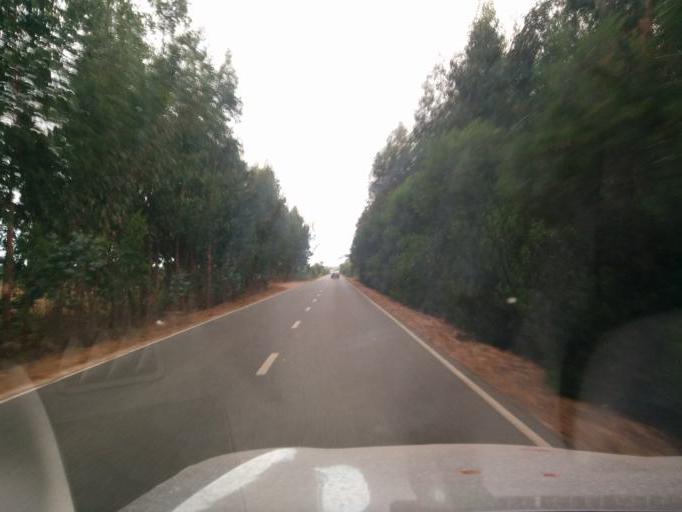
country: PT
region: Beja
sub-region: Odemira
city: Sao Teotonio
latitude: 37.5652
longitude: -8.7363
